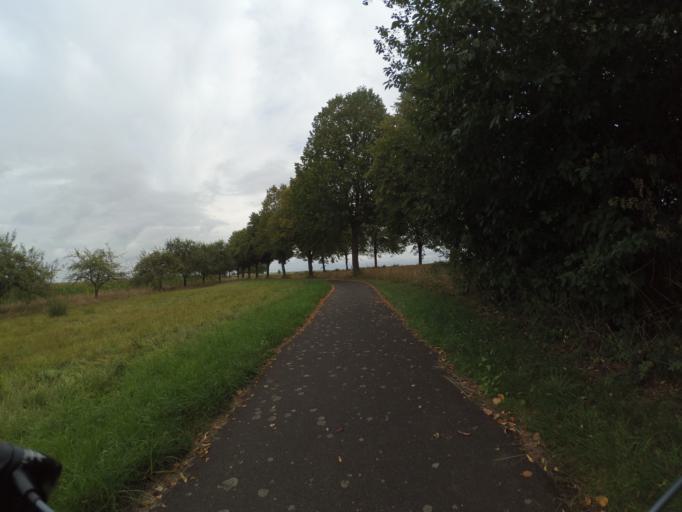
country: DE
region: Rheinland-Pfalz
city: Beilingen
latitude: 49.9430
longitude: 6.6512
